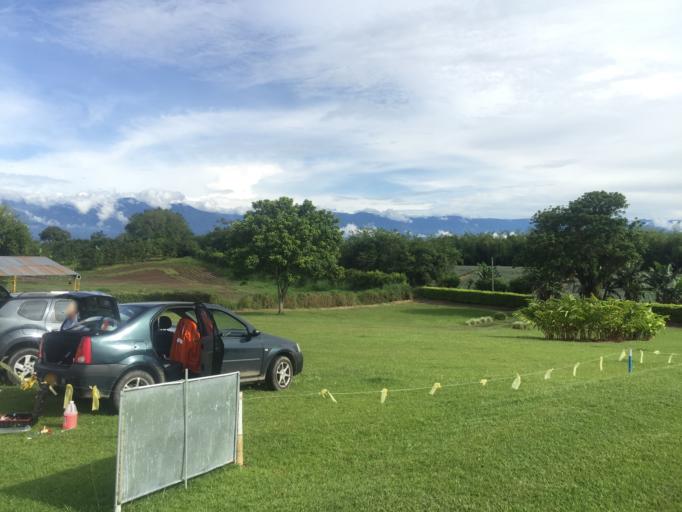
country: CO
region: Quindio
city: La Tebaida
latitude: 4.4748
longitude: -75.8410
